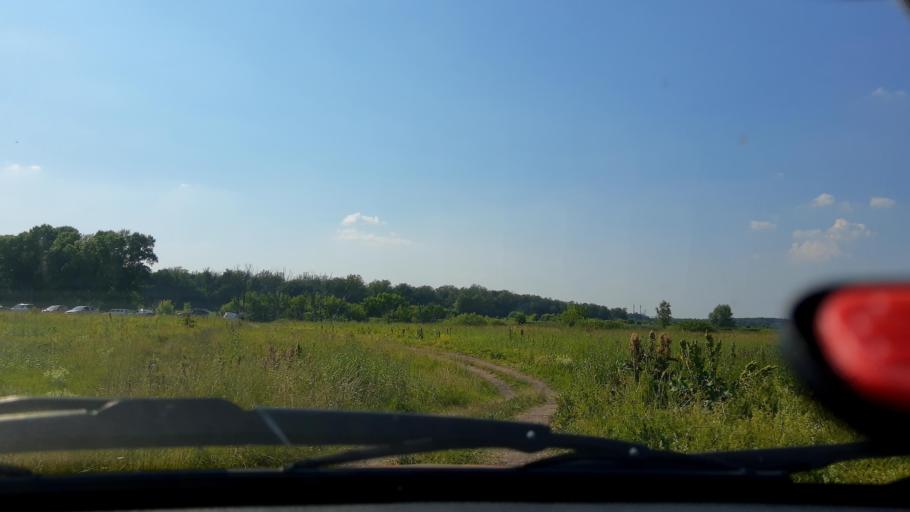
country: RU
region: Bashkortostan
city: Kabakovo
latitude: 54.7463
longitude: 56.1798
